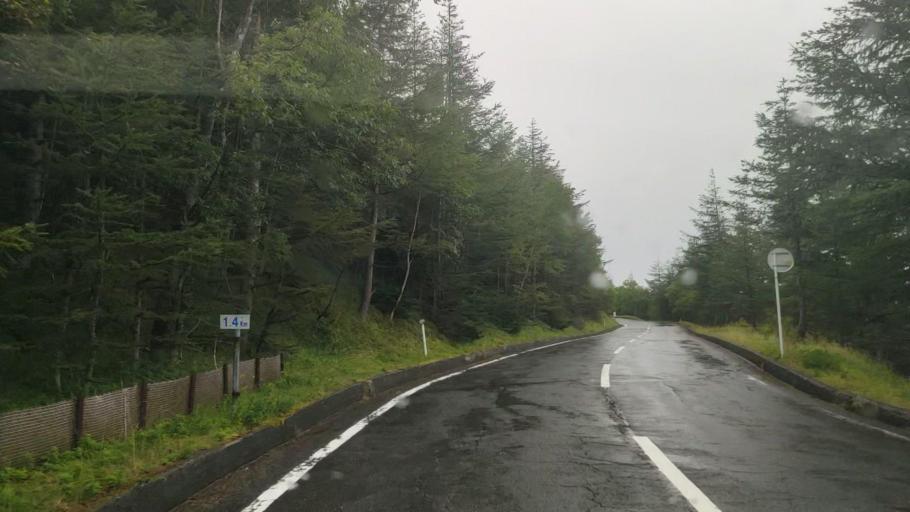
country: JP
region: Yamanashi
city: Fujikawaguchiko
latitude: 35.3351
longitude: 138.7309
